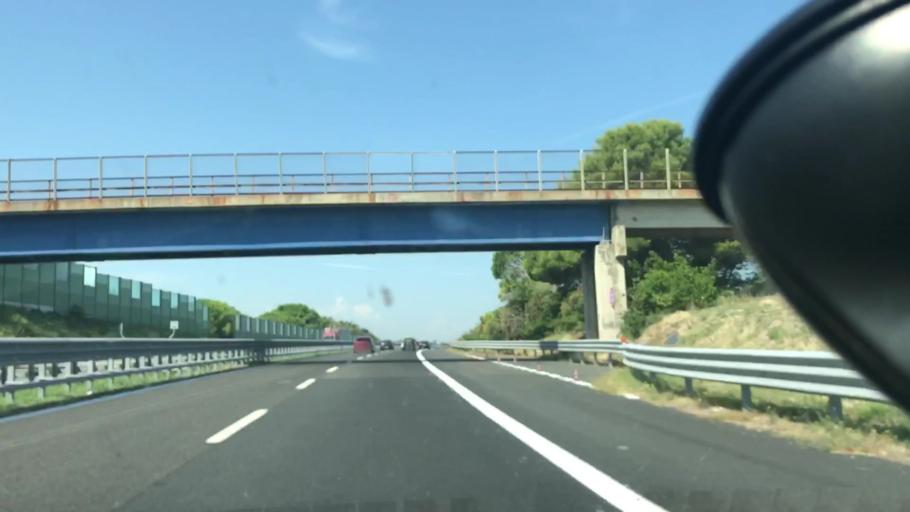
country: IT
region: Molise
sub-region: Provincia di Campobasso
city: Petacciato
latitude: 42.0166
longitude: 14.9077
